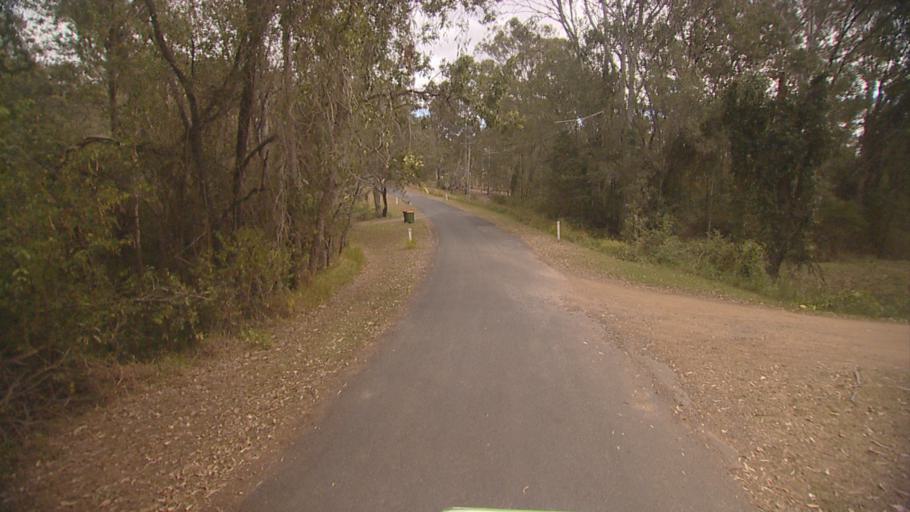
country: AU
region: Queensland
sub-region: Logan
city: Cedar Vale
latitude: -27.8549
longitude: 153.0664
